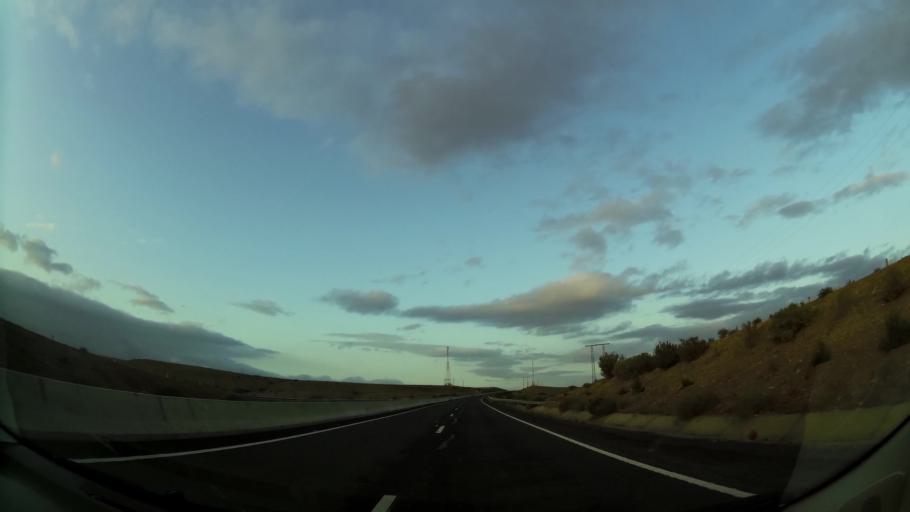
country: MA
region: Oriental
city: Taourirt
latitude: 34.5453
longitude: -2.9041
